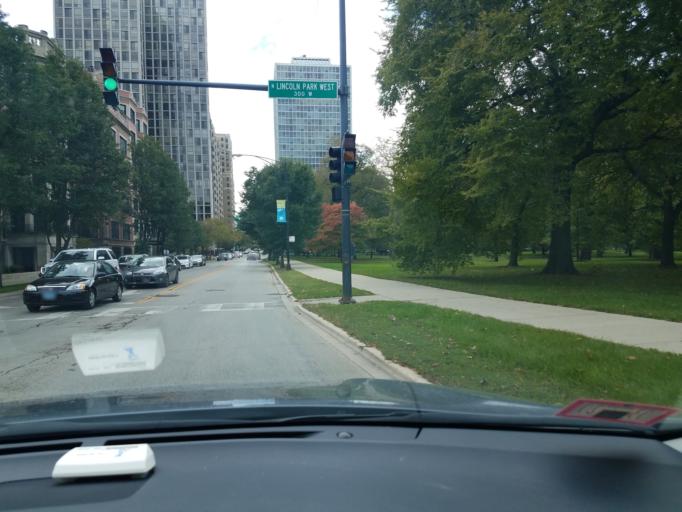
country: US
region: Illinois
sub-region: Cook County
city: Chicago
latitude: 41.9257
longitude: -87.6365
